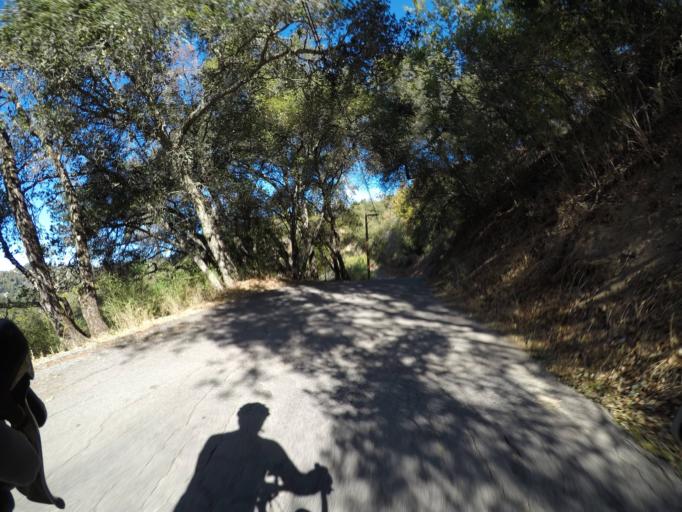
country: US
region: California
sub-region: Santa Clara County
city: Lexington Hills
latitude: 37.1266
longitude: -121.9884
